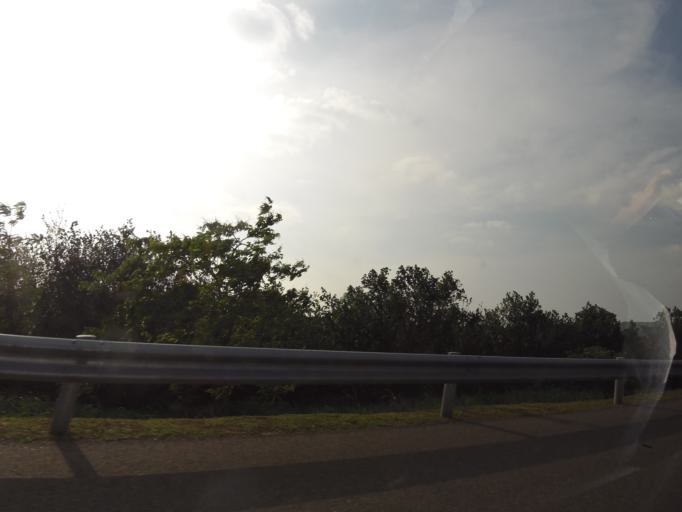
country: LK
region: Western
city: Katunayaka
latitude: 7.1230
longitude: 79.8730
